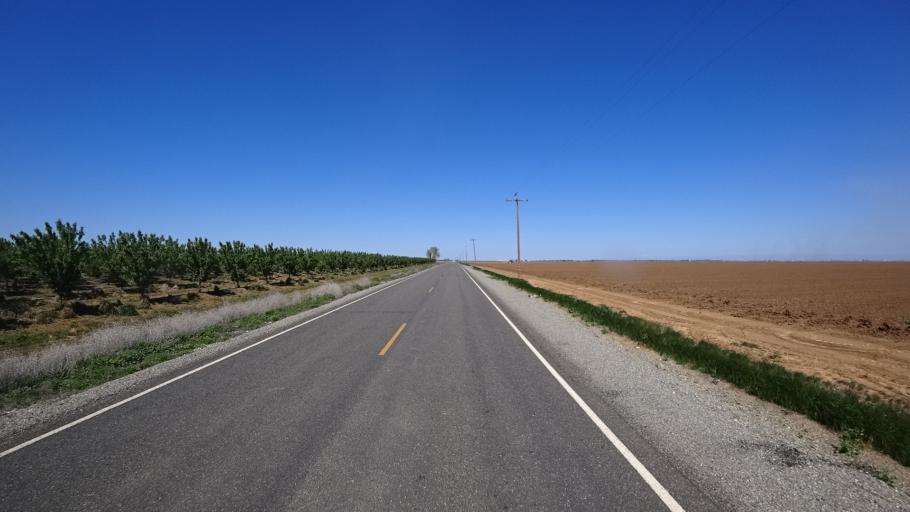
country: US
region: California
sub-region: Glenn County
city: Willows
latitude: 39.4552
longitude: -122.2487
